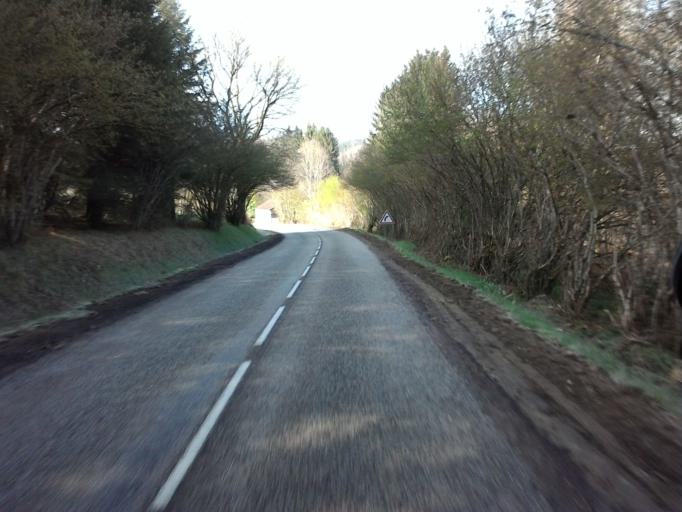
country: FR
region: Bourgogne
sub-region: Departement de la Cote-d'Or
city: Saulieu
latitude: 47.2470
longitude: 4.0638
